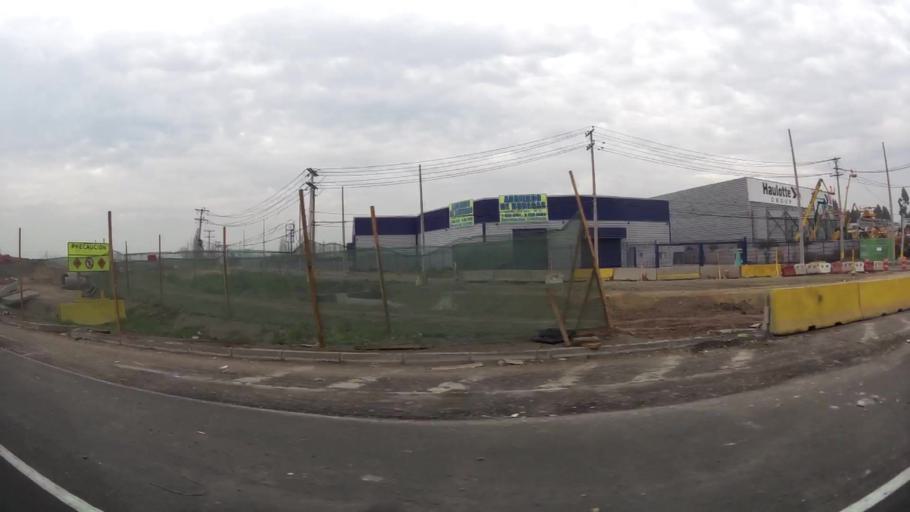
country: CL
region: Santiago Metropolitan
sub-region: Provincia de Chacabuco
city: Chicureo Abajo
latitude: -33.2745
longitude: -70.7413
